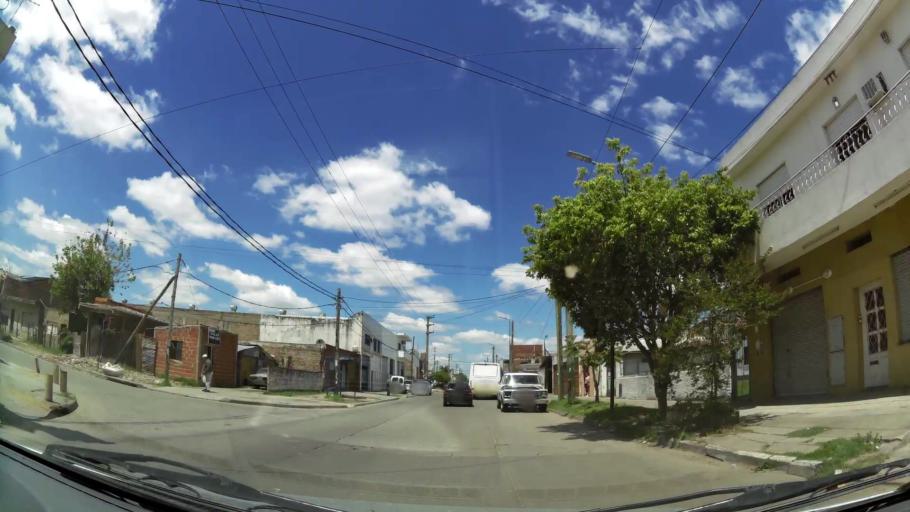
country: AR
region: Buenos Aires
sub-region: Partido de Lanus
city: Lanus
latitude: -34.7232
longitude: -58.4274
